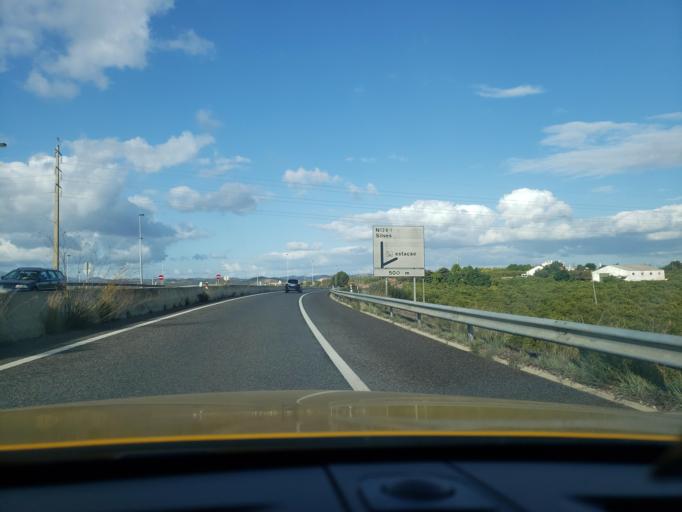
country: PT
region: Faro
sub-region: Silves
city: Silves
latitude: 37.1767
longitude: -8.4441
